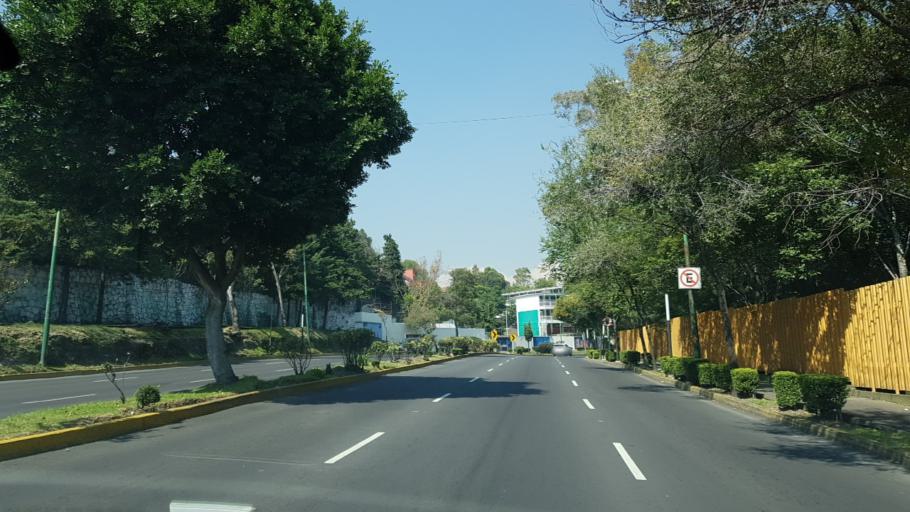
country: MX
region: Mexico City
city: Alvaro Obregon
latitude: 19.3531
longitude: -99.2118
